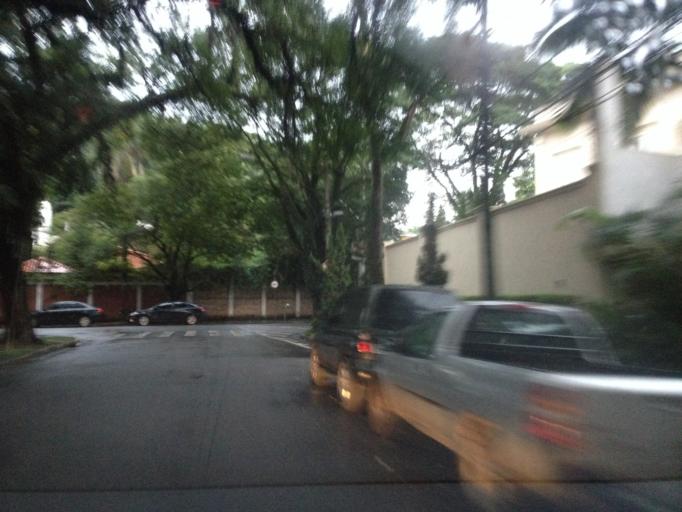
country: BR
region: Sao Paulo
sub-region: Sao Paulo
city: Sao Paulo
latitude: -23.5790
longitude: -46.6640
